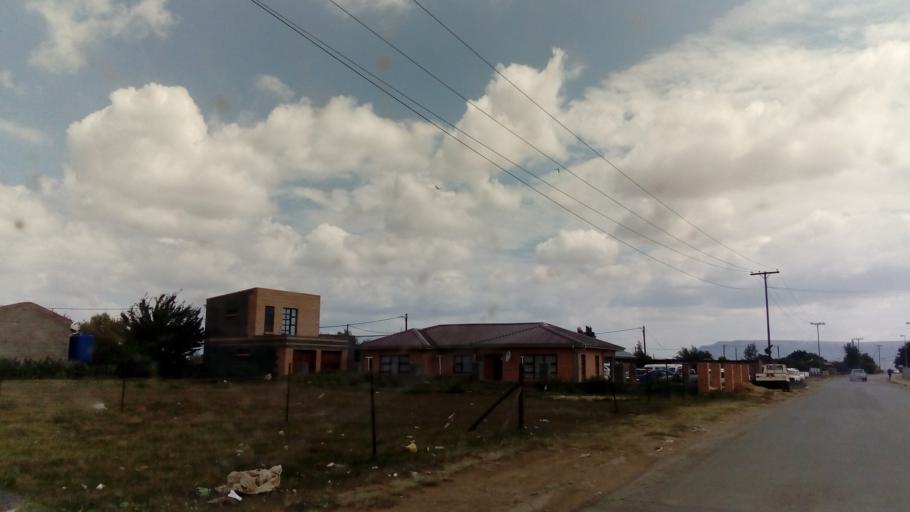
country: LS
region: Maseru
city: Maseru
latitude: -29.3806
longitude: 27.5305
